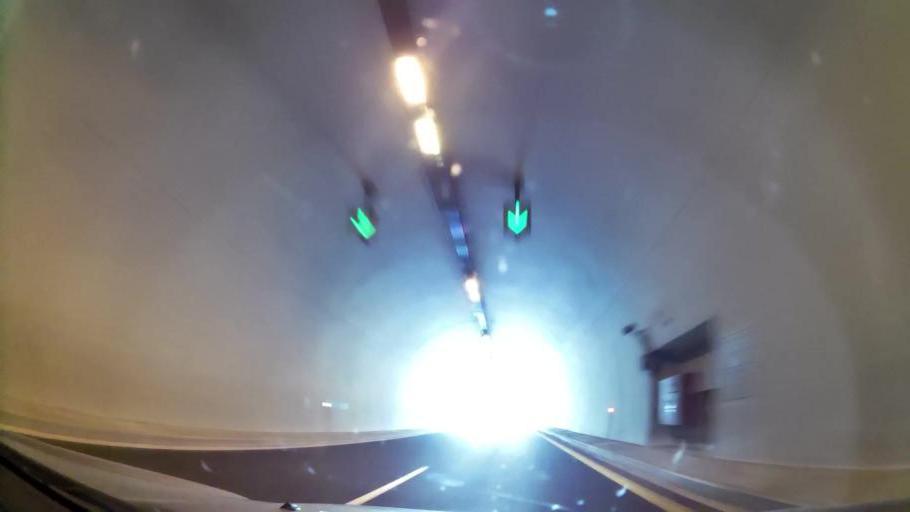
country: GR
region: Central Macedonia
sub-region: Nomos Imathias
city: Rizomata
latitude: 40.3803
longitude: 22.1017
